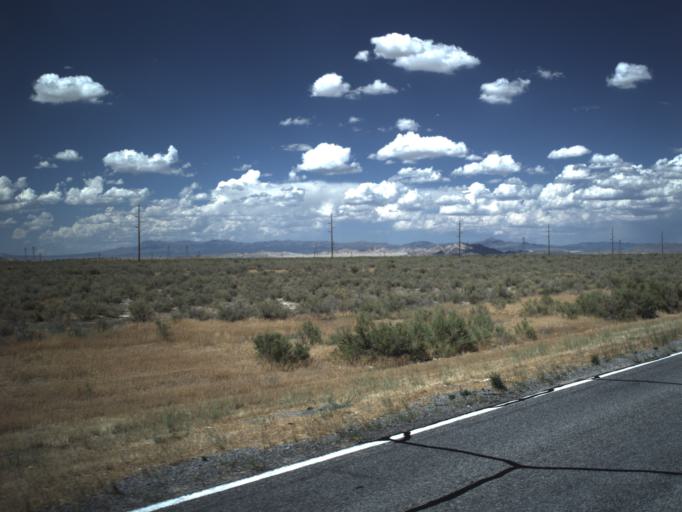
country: US
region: Utah
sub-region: Millard County
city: Delta
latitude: 39.4685
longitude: -112.4261
